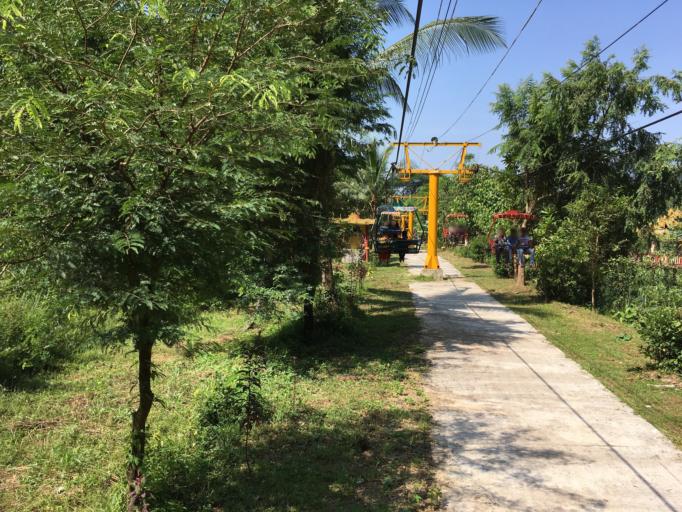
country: MM
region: Kayin
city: Hpa-an
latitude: 16.8097
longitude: 97.6751
